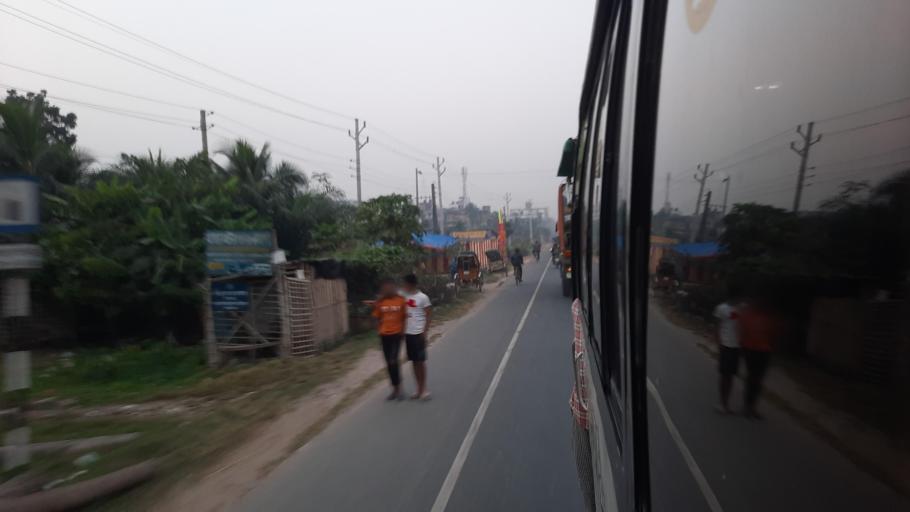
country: BD
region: Khulna
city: Jessore
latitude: 23.1683
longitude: 89.1931
